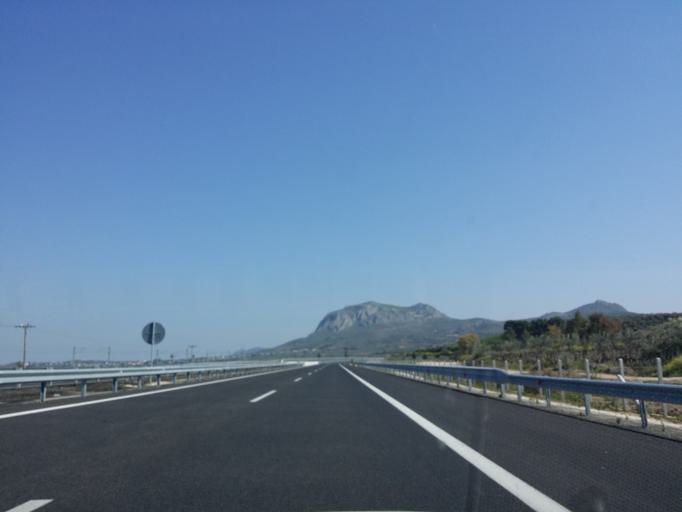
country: GR
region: Peloponnese
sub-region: Nomos Korinthias
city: Assos
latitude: 37.9182
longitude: 22.8236
